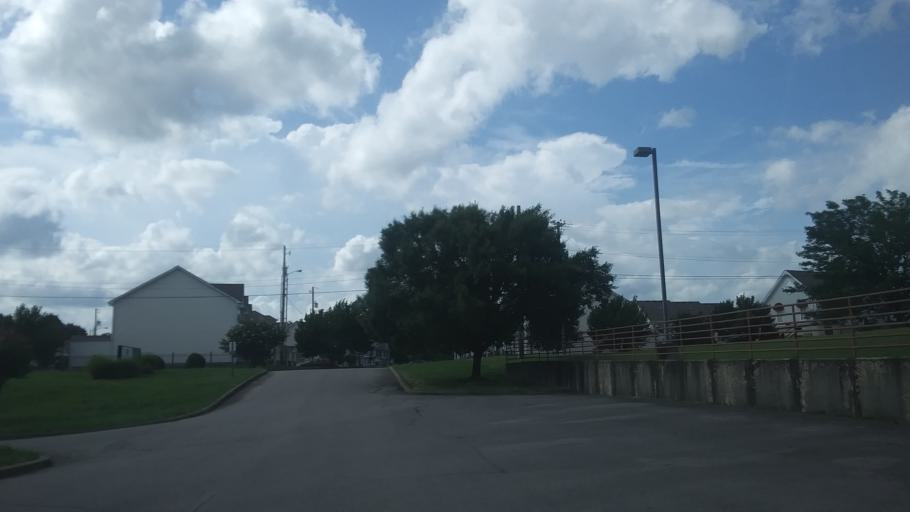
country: US
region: Tennessee
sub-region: Rutherford County
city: La Vergne
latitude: 36.0880
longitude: -86.6514
